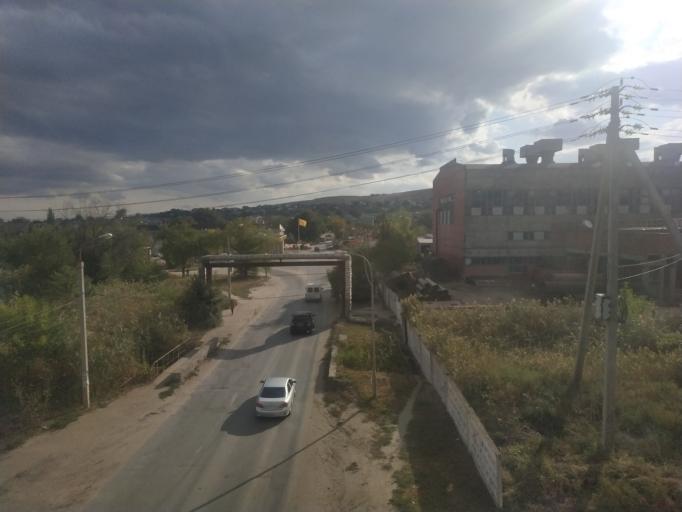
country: RU
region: Volgograd
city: Krasnoslobodsk
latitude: 48.5068
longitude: 44.5475
